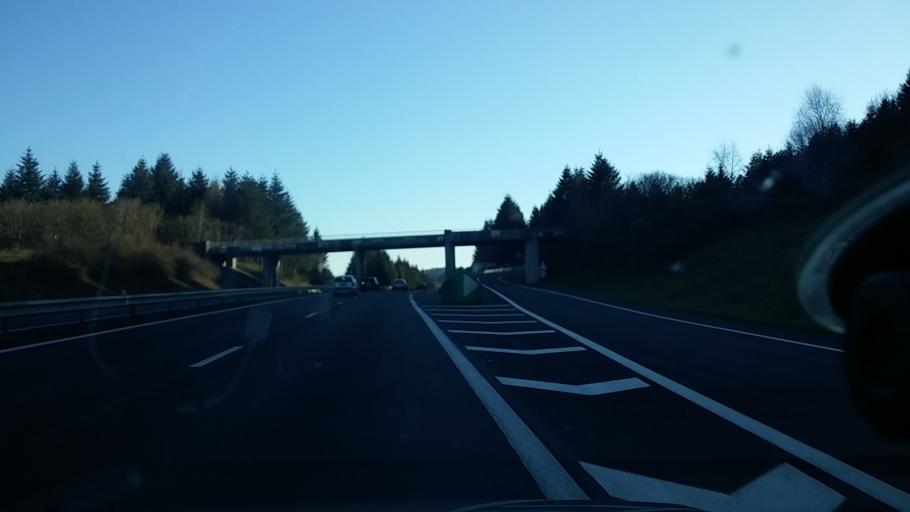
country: FR
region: Limousin
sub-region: Departement de la Haute-Vienne
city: Razes
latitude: 46.0266
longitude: 1.3456
